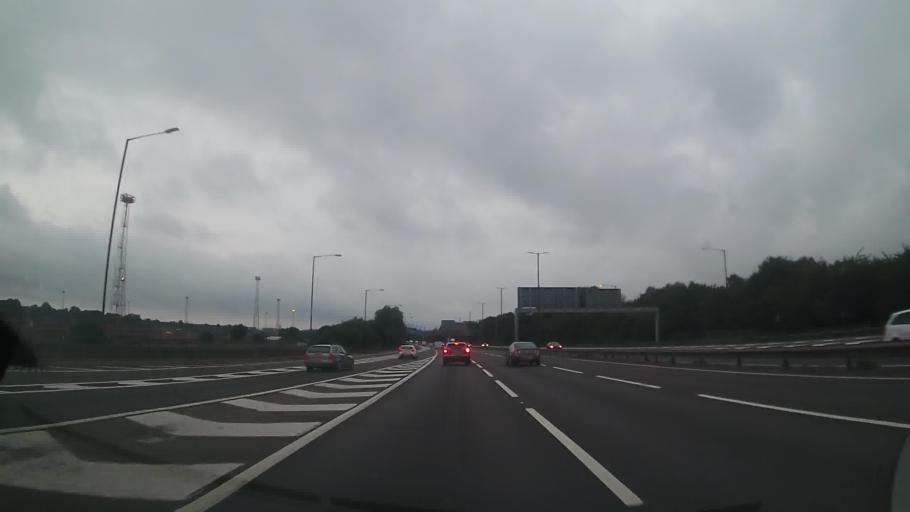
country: GB
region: England
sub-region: Walsall
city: Walsall
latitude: 52.5587
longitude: -1.9755
